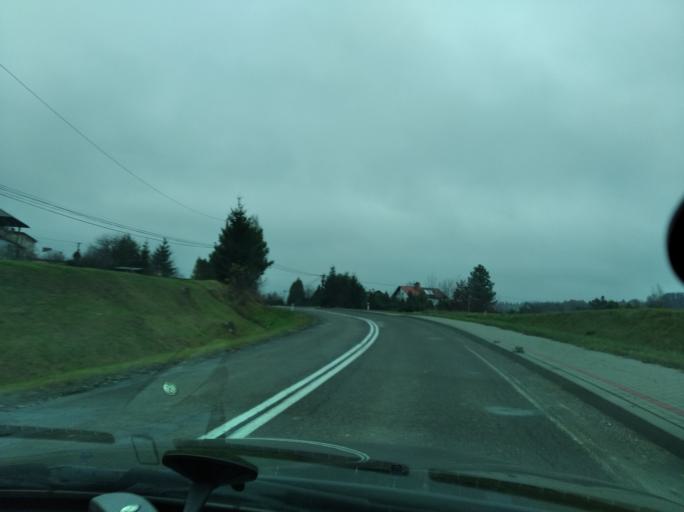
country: PL
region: Subcarpathian Voivodeship
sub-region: Powiat przeworski
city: Jawornik Polski
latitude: 49.8709
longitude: 22.2461
